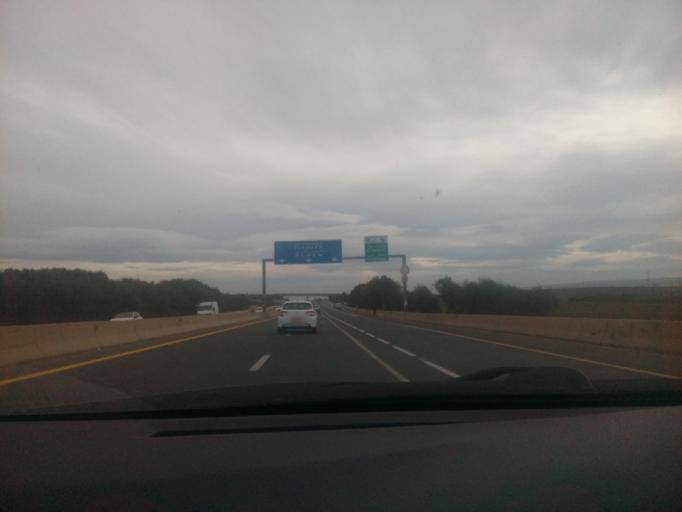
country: DZ
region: Oran
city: Sidi ech Chahmi
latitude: 35.5766
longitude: -0.5616
